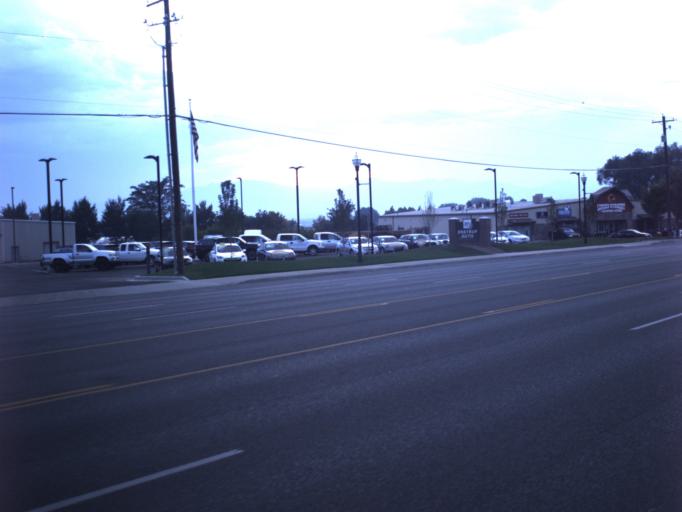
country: US
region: Utah
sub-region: Utah County
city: Lindon
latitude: 40.3459
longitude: -111.7244
